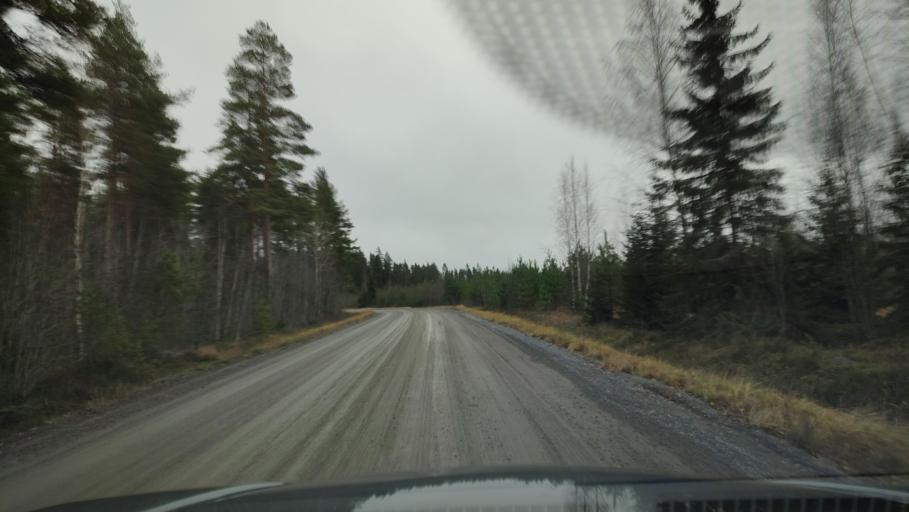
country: FI
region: Southern Ostrobothnia
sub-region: Suupohja
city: Karijoki
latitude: 62.1253
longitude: 21.5960
